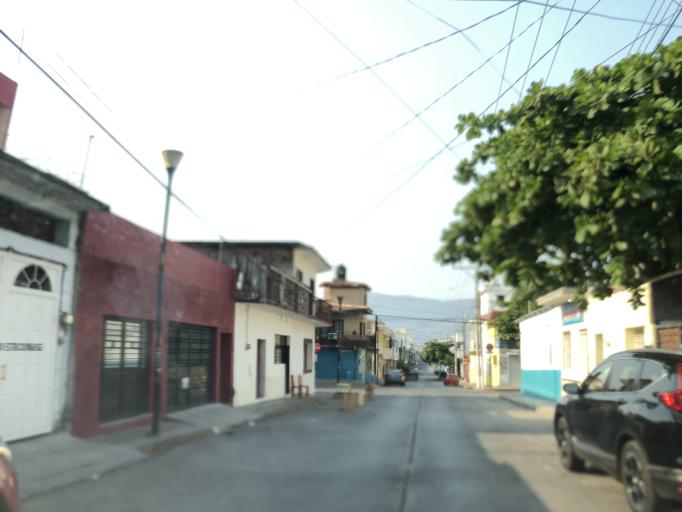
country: MX
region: Chiapas
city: Tuxtla Gutierrez
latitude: 16.7490
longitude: -93.1222
